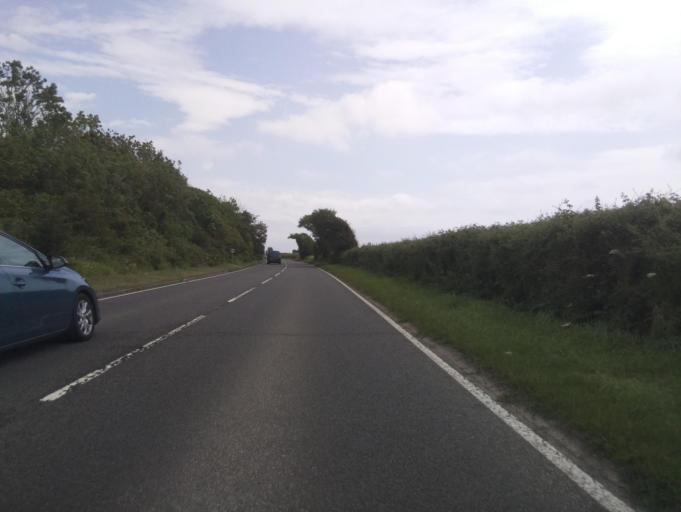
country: GB
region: Wales
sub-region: Vale of Glamorgan
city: Llantwit Major
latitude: 51.3999
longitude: -3.4459
